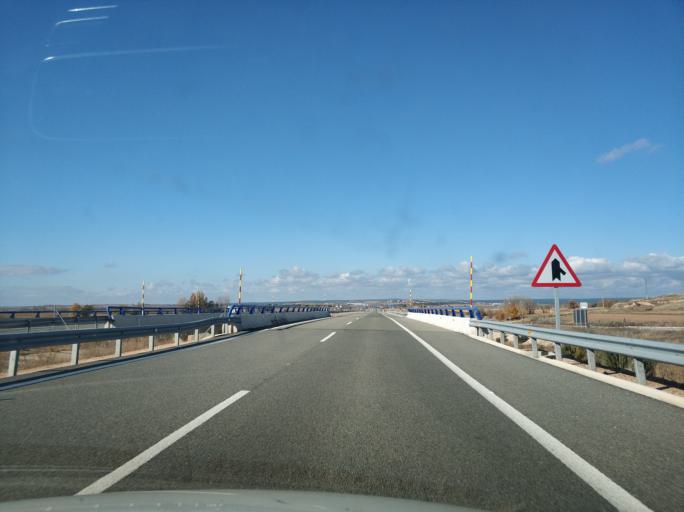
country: ES
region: Castille and Leon
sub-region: Provincia de Soria
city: Frechilla de Almazan
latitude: 41.4465
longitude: -2.5066
